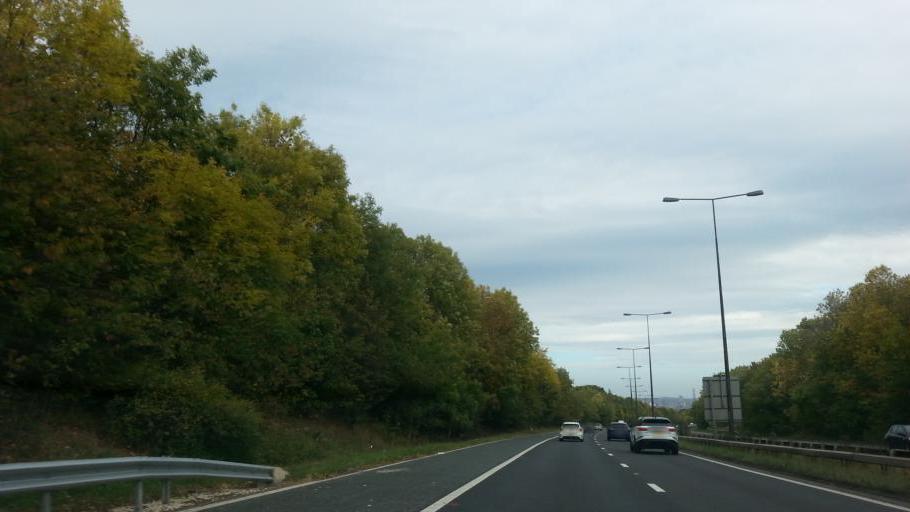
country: GB
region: England
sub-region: City and Borough of Leeds
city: Gildersome
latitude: 53.7540
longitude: -1.6146
